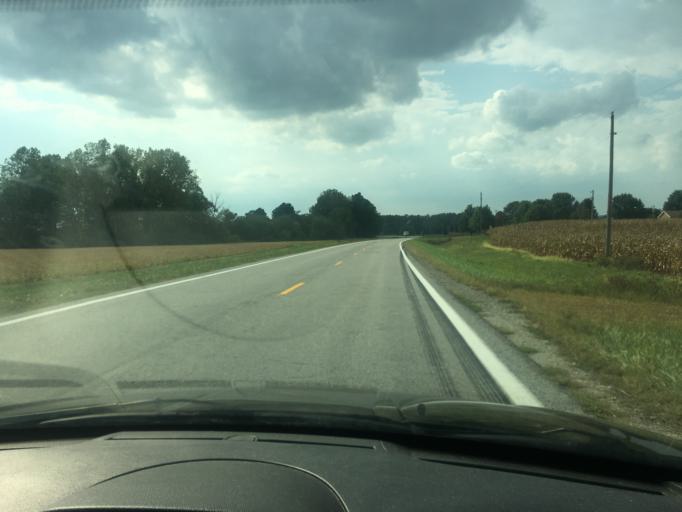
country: US
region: Ohio
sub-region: Champaign County
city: Urbana
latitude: 40.1571
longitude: -83.7777
